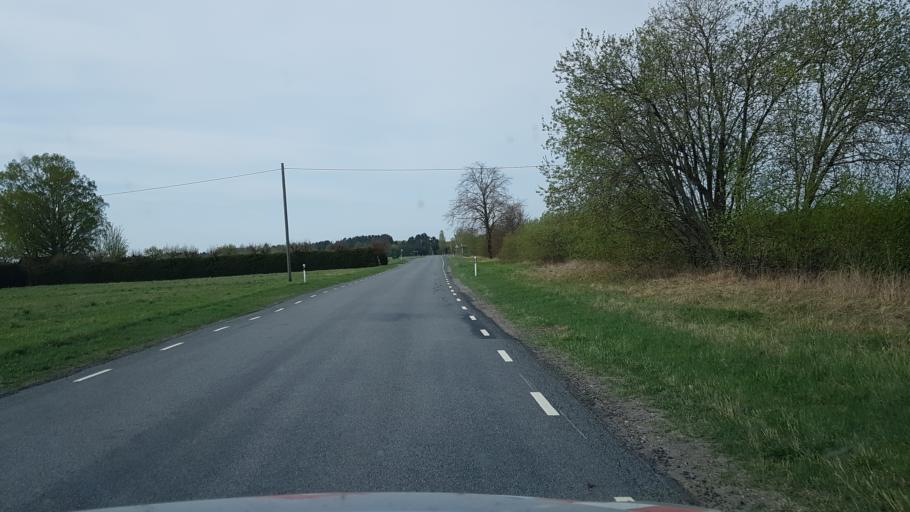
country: EE
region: Paernumaa
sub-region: Audru vald
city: Audru
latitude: 58.3630
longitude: 24.2624
